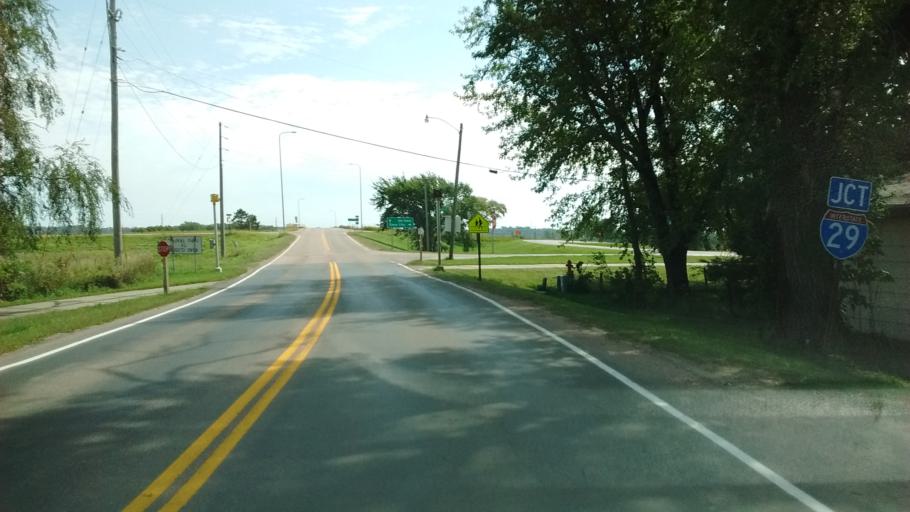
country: US
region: South Dakota
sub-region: Union County
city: North Sioux City
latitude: 42.5502
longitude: -96.5119
